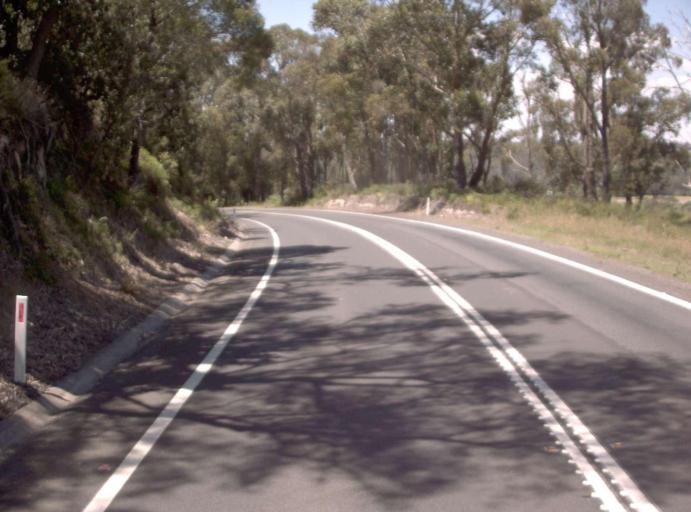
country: AU
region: Victoria
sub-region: East Gippsland
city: Lakes Entrance
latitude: -37.7080
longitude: 148.6996
